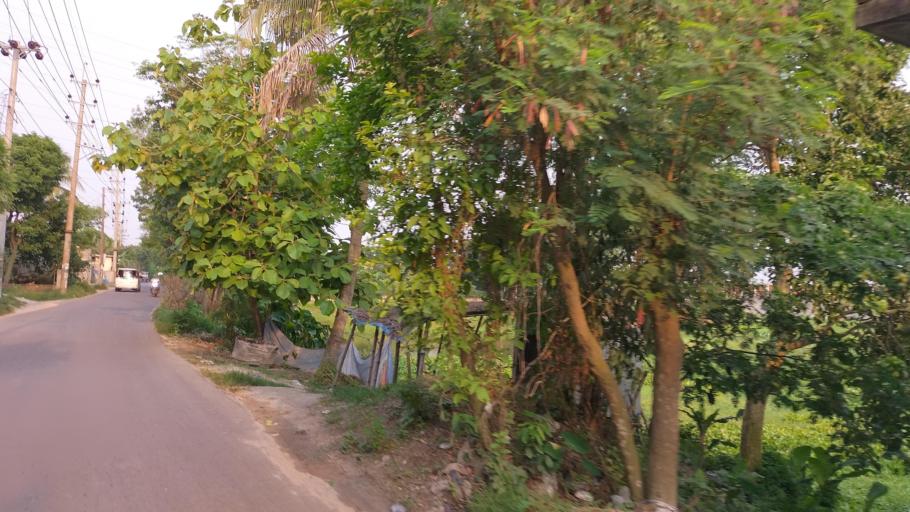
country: BD
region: Dhaka
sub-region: Dhaka
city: Dhaka
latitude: 23.6540
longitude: 90.3445
